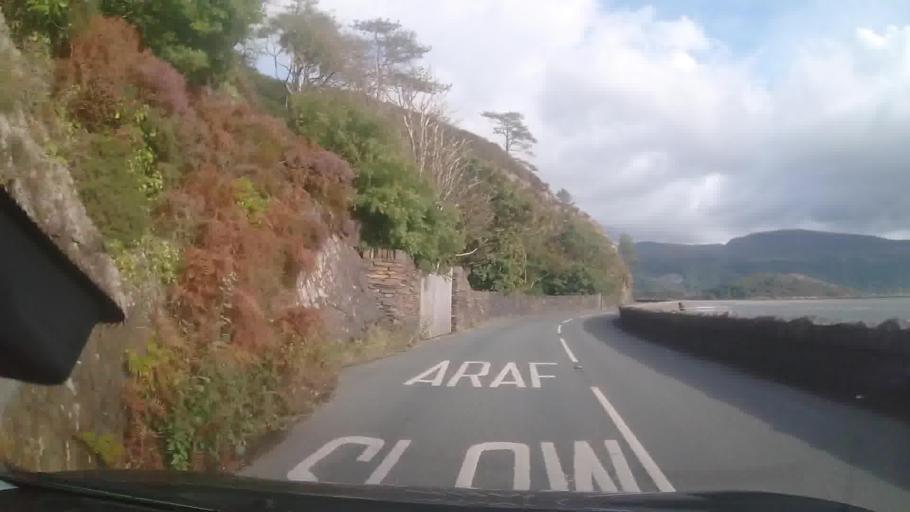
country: GB
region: Wales
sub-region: Gwynedd
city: Barmouth
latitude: 52.7220
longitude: -4.0407
